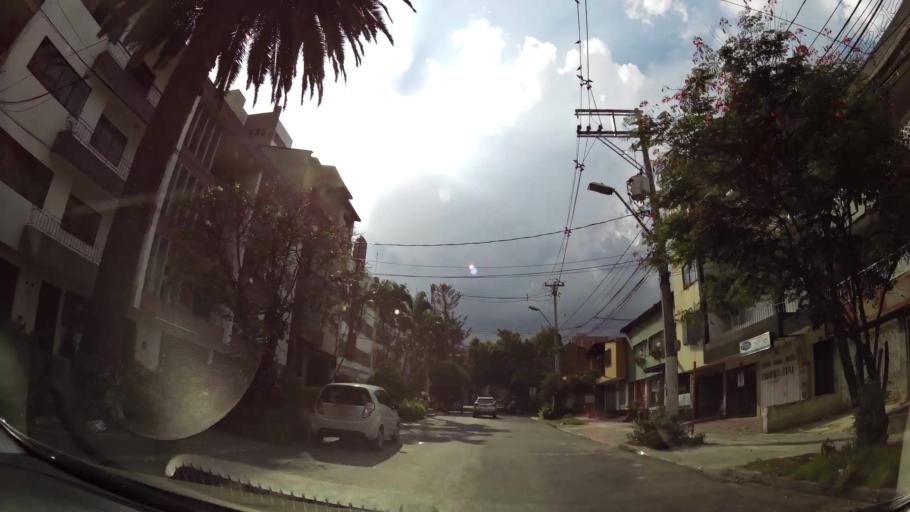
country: CO
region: Antioquia
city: Medellin
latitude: 6.2500
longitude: -75.5894
